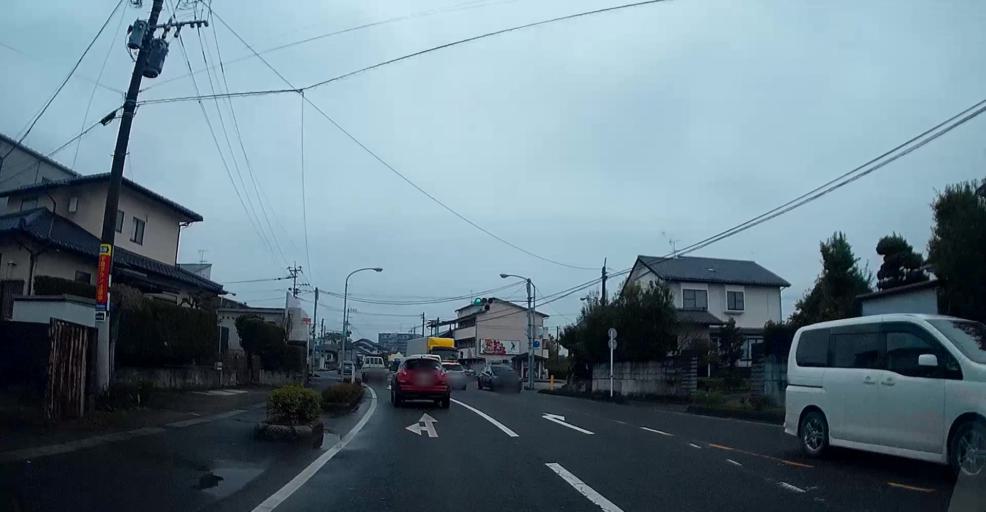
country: JP
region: Kumamoto
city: Kumamoto
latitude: 32.7445
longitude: 130.7396
